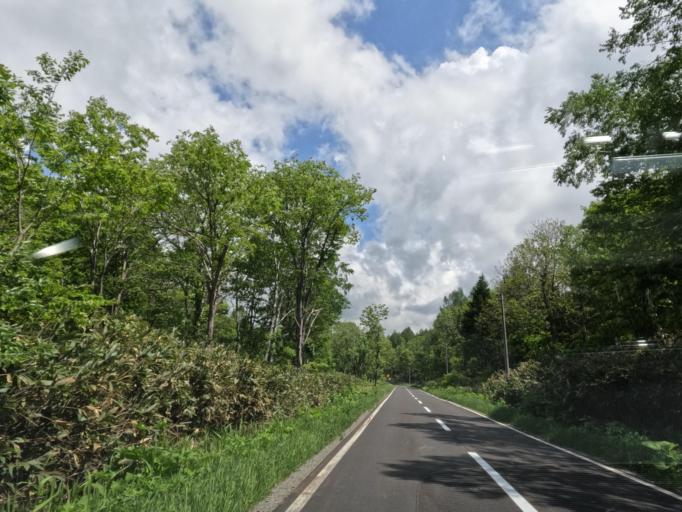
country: JP
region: Hokkaido
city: Takikawa
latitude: 43.5434
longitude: 141.6331
